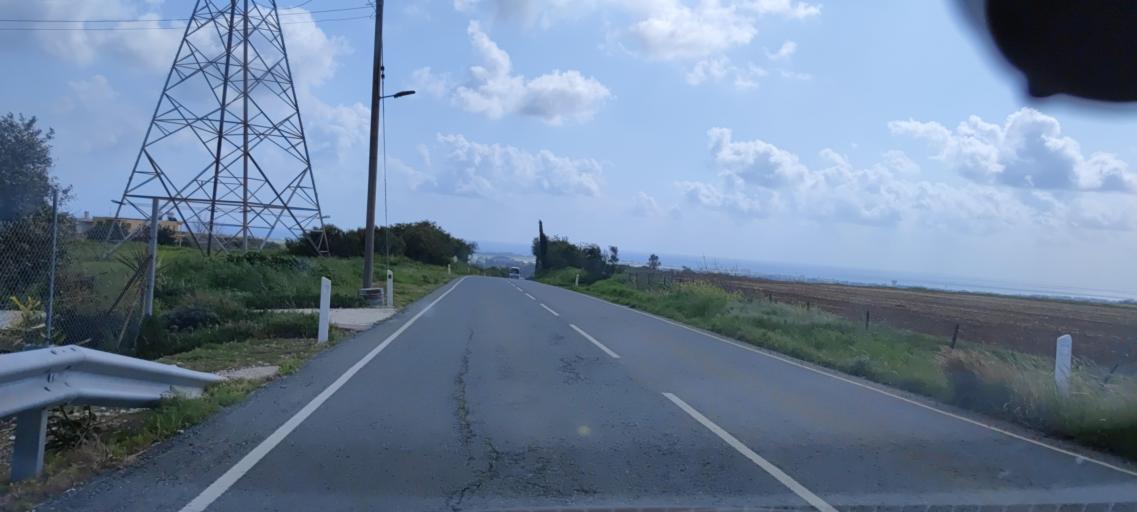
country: CY
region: Pafos
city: Paphos
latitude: 34.7424
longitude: 32.4980
